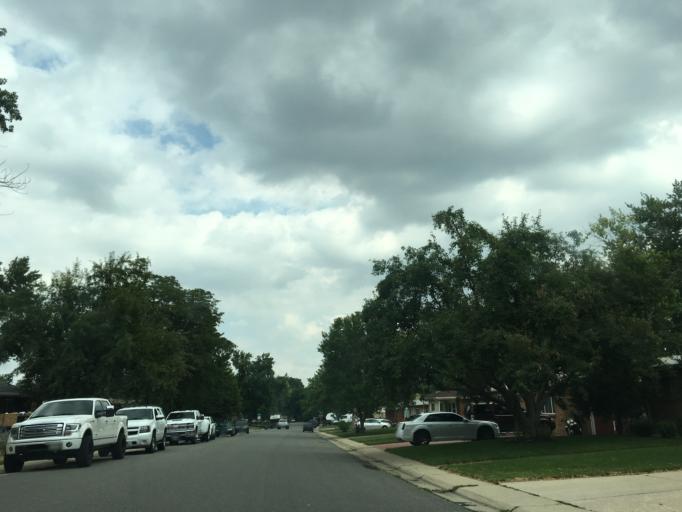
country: US
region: Colorado
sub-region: Arapahoe County
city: Sheridan
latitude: 39.6774
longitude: -105.0368
